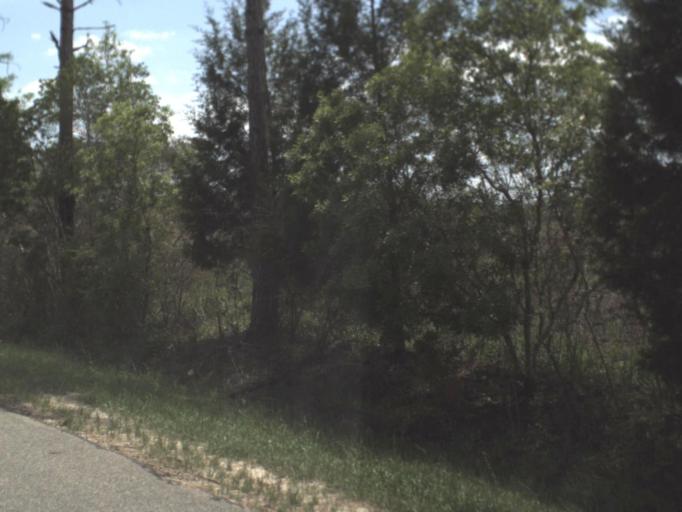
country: US
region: Florida
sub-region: Calhoun County
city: Blountstown
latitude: 30.4677
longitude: -85.0801
